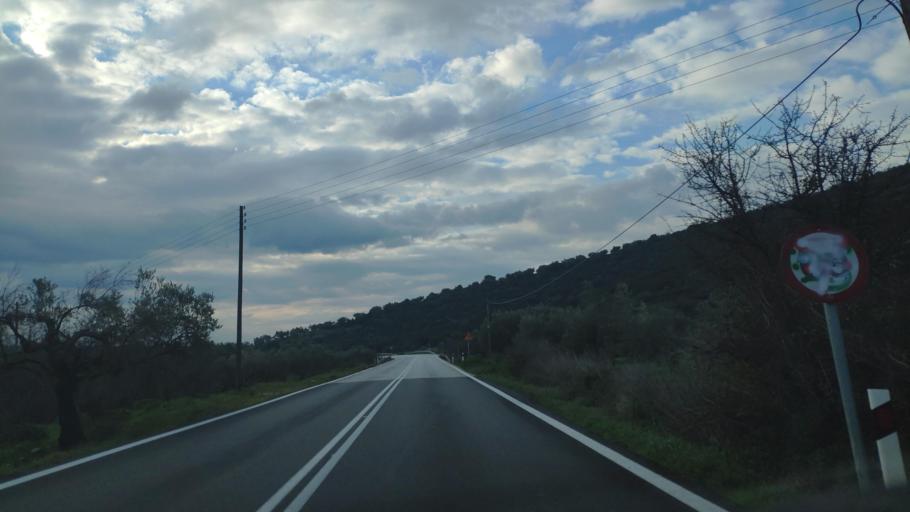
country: GR
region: Peloponnese
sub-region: Nomos Argolidos
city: Koutsopodi
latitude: 37.7421
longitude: 22.7346
